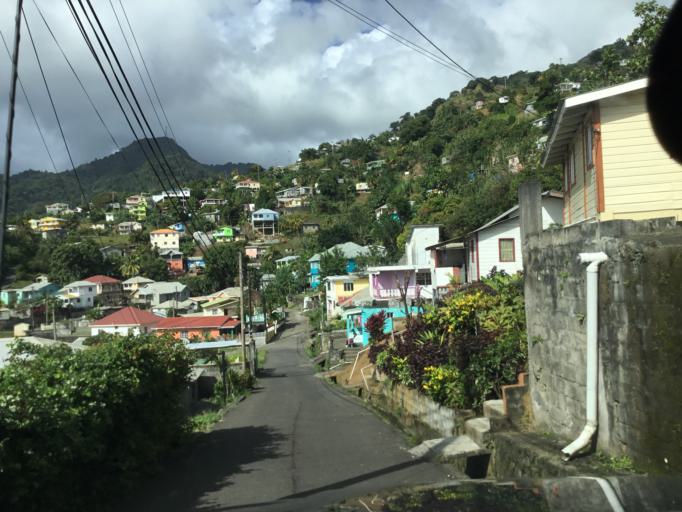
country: VC
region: Saint George
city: Kingstown
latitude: 13.1656
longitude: -61.2181
